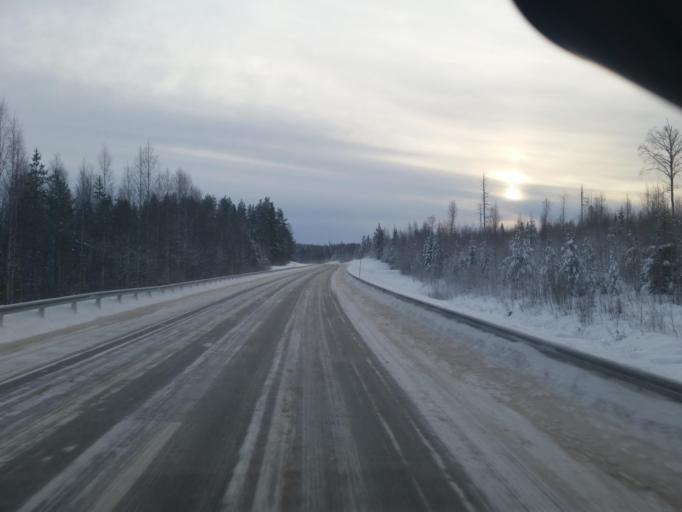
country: SE
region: Norrbotten
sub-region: Pitea Kommun
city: Norrfjarden
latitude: 65.6272
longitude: 21.3969
